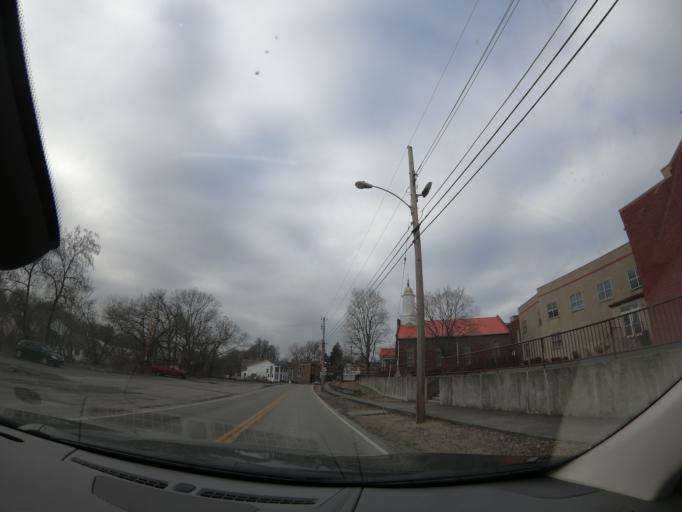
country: US
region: Kentucky
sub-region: Spencer County
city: Taylorsville
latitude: 37.9109
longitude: -85.3174
